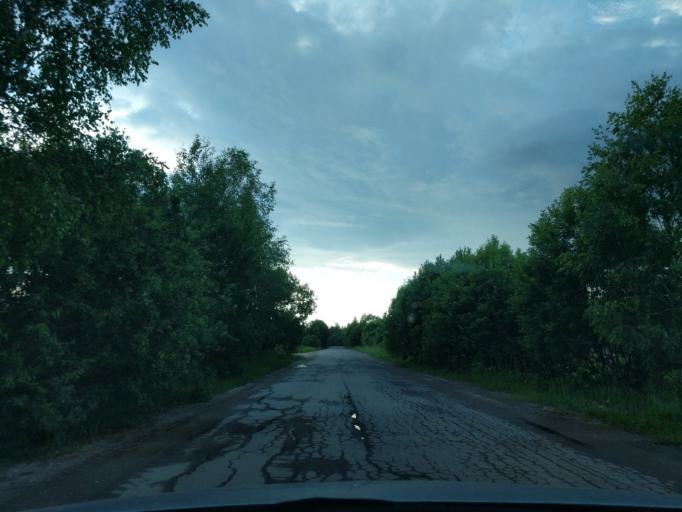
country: RU
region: Kaluga
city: Myatlevo
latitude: 54.8566
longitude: 35.5795
